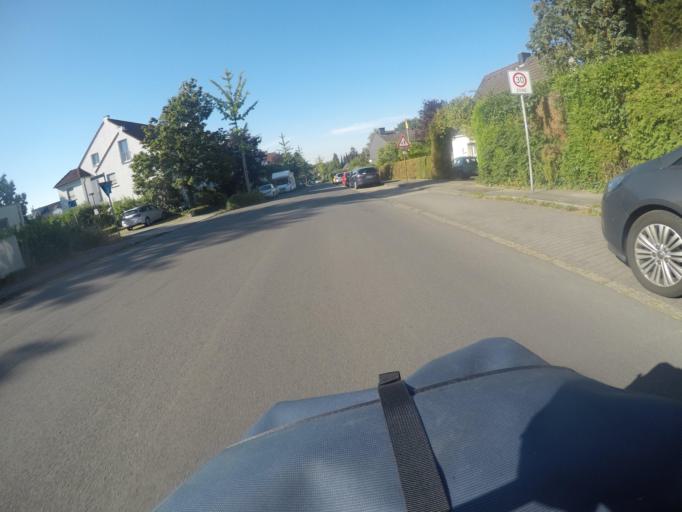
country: DE
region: North Rhine-Westphalia
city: Haan
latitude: 51.1863
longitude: 7.0047
